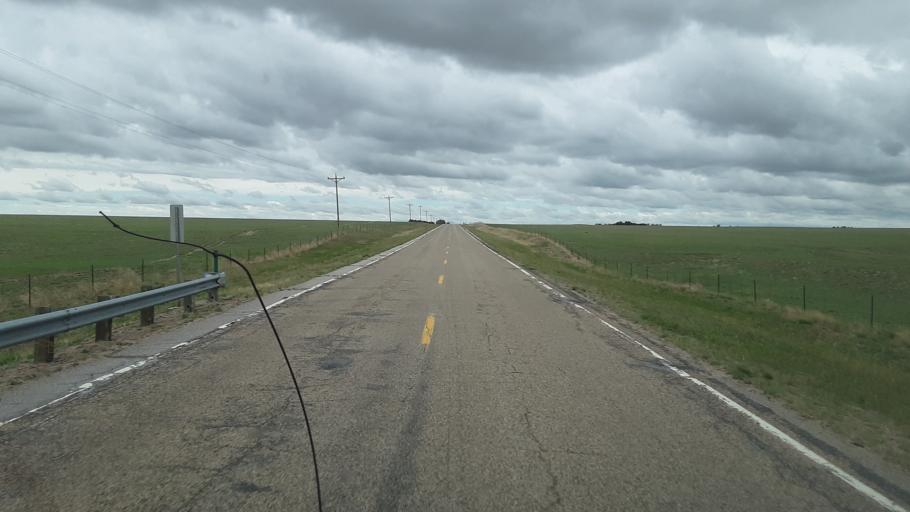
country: US
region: Colorado
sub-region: El Paso County
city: Ellicott
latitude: 38.8398
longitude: -103.9537
